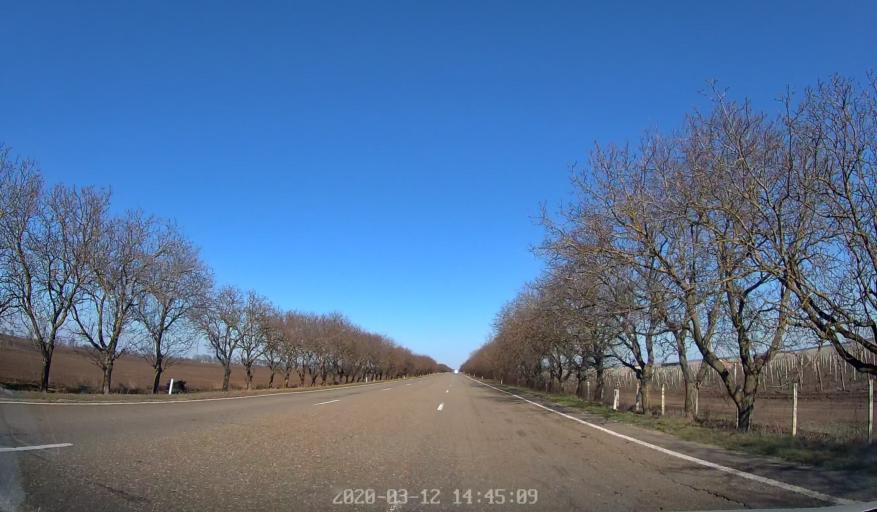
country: MD
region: Criuleni
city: Criuleni
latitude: 47.2149
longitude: 29.1045
